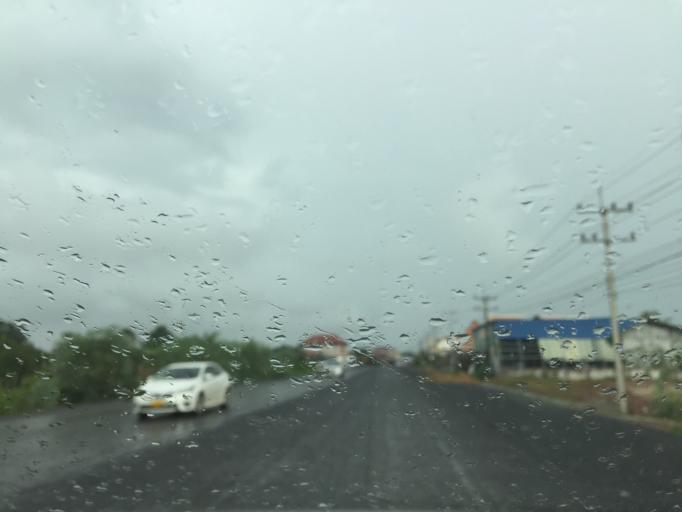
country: LA
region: Attapu
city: Attapu
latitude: 14.8235
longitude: 106.8103
